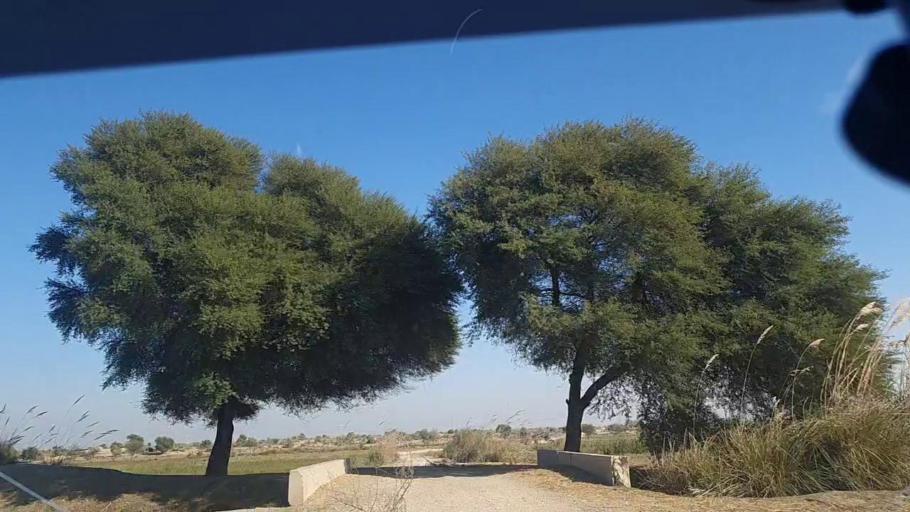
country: PK
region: Sindh
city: Khanpur
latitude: 27.6484
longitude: 69.3917
